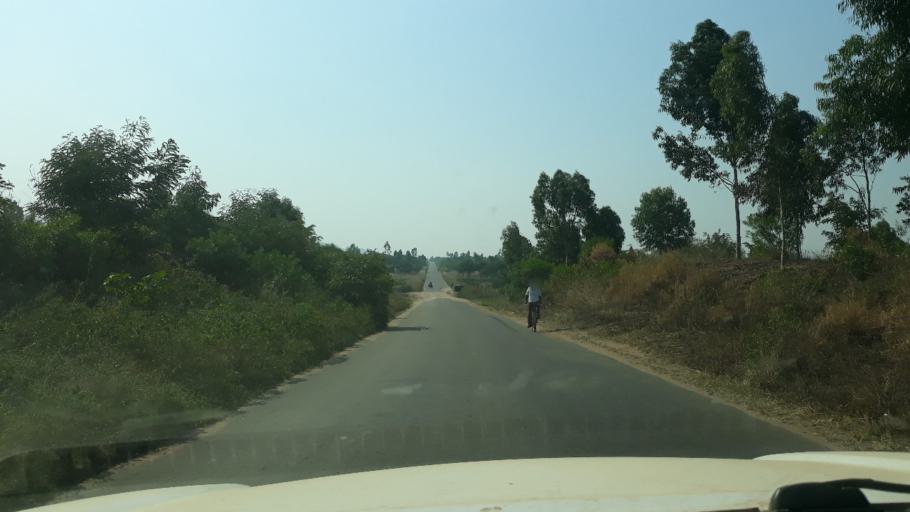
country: BI
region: Cibitoke
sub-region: Commune of Buganda
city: Buganda
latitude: -3.1603
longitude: 29.1492
